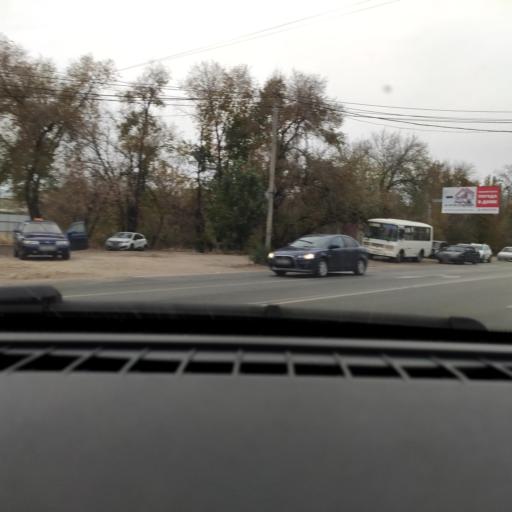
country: RU
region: Voronezj
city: Maslovka
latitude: 51.5990
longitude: 39.2525
